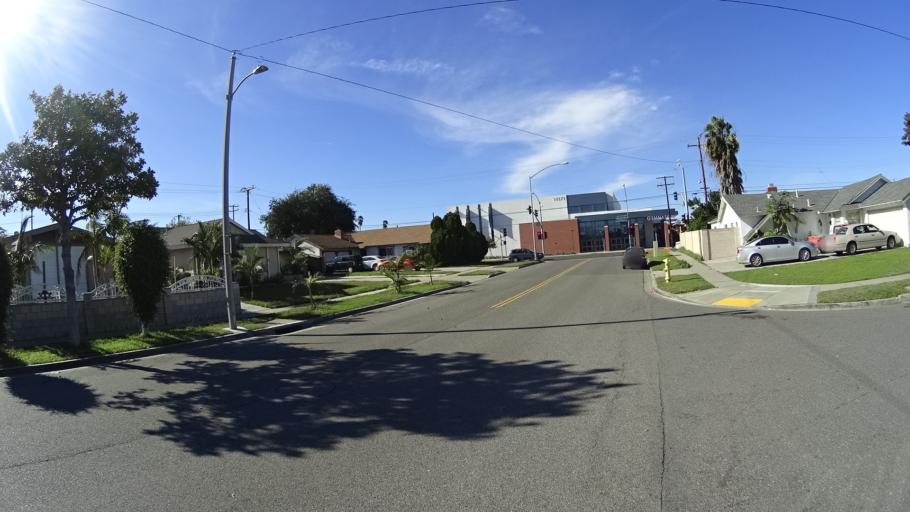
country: US
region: California
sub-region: Orange County
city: Midway City
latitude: 33.7561
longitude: -117.9804
